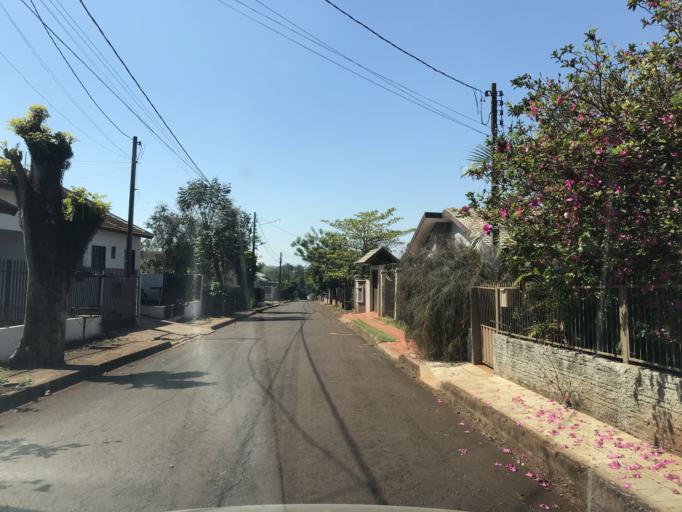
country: BR
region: Parana
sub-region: Palotina
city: Palotina
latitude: -24.3011
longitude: -53.8325
